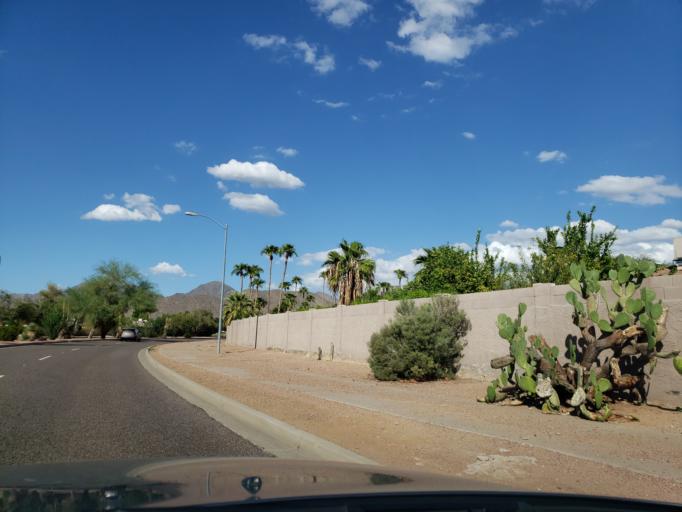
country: US
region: Arizona
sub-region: Maricopa County
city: Scottsdale
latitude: 33.5845
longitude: -111.8521
